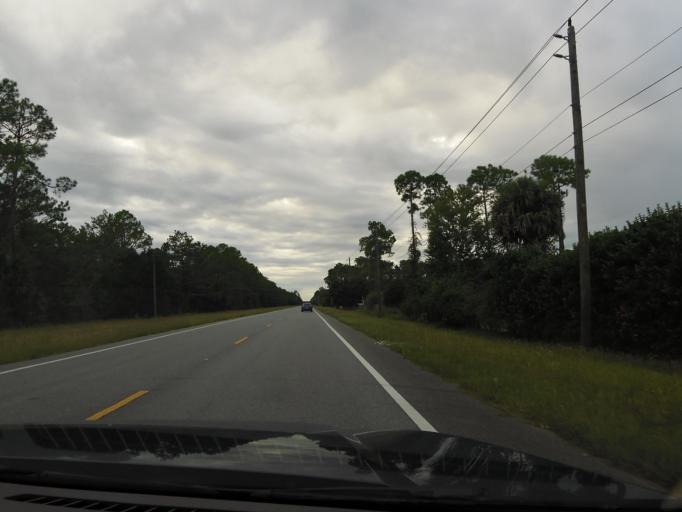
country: US
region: Florida
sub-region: Flagler County
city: Bunnell
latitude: 29.4975
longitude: -81.2330
